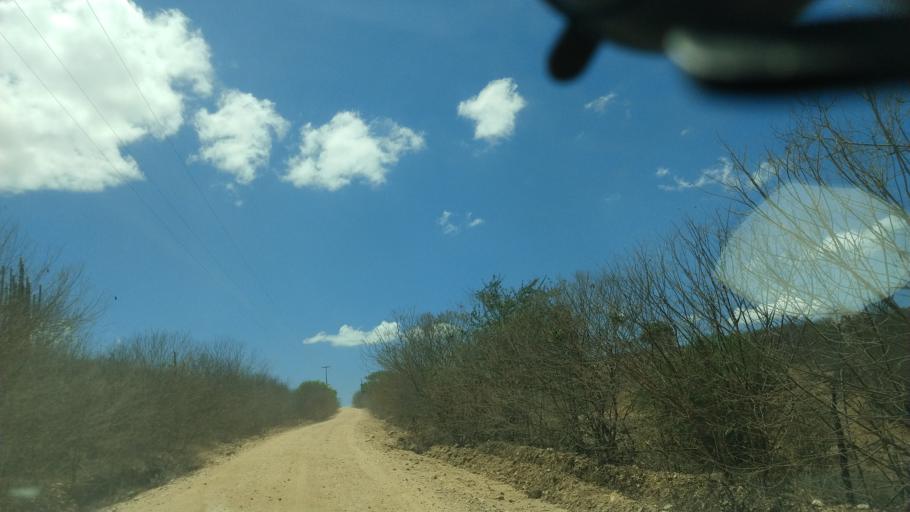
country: BR
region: Rio Grande do Norte
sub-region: Cerro Cora
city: Cerro Cora
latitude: -6.0154
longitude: -36.3280
